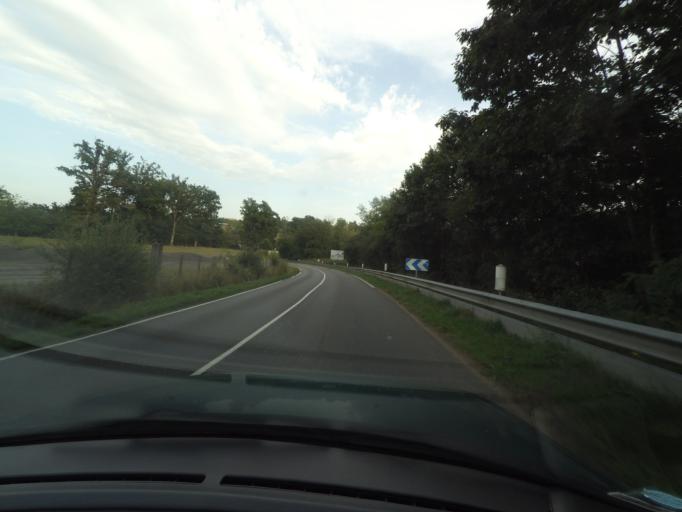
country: FR
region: Limousin
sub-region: Departement de la Haute-Vienne
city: Saint-Priest-sous-Aixe
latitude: 45.8010
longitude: 1.1052
